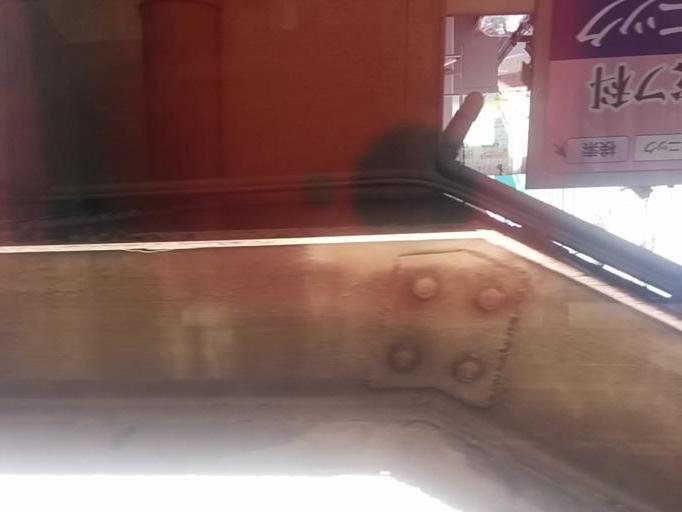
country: JP
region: Nara
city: Nara-shi
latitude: 34.6942
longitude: 135.7831
